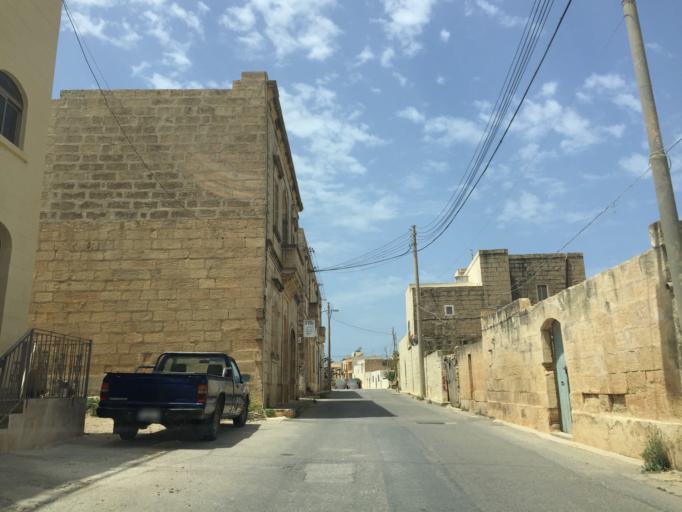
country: MT
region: Ix-Xaghra
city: Xaghra
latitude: 36.0483
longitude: 14.2578
